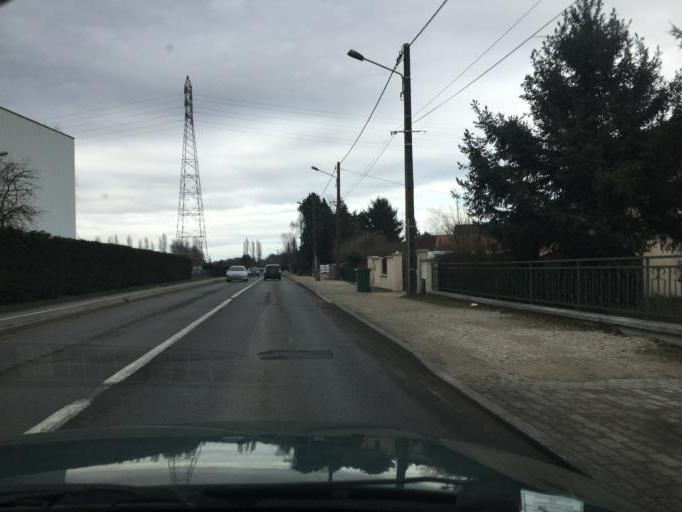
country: FR
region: Centre
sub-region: Departement du Loiret
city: Fleury-les-Aubrais
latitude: 47.9460
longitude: 1.9214
